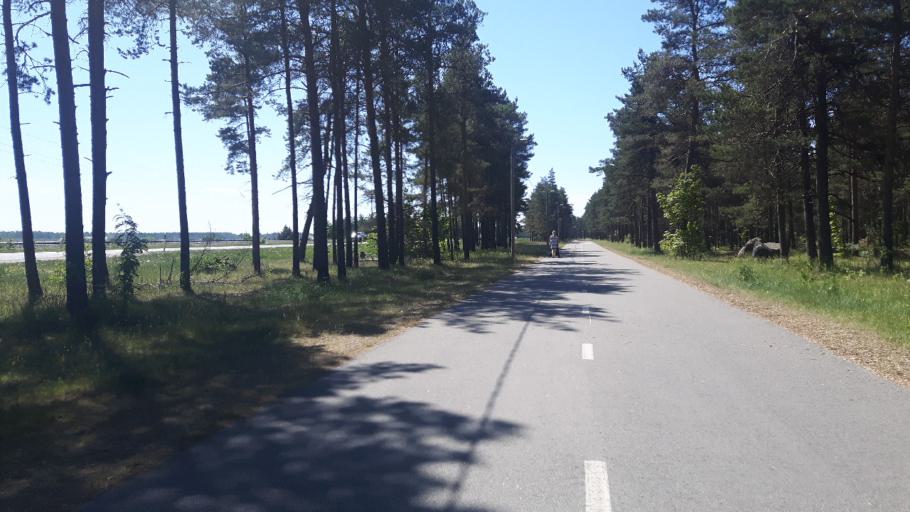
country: EE
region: Harju
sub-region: Saku vald
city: Saku
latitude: 59.3606
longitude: 24.7153
